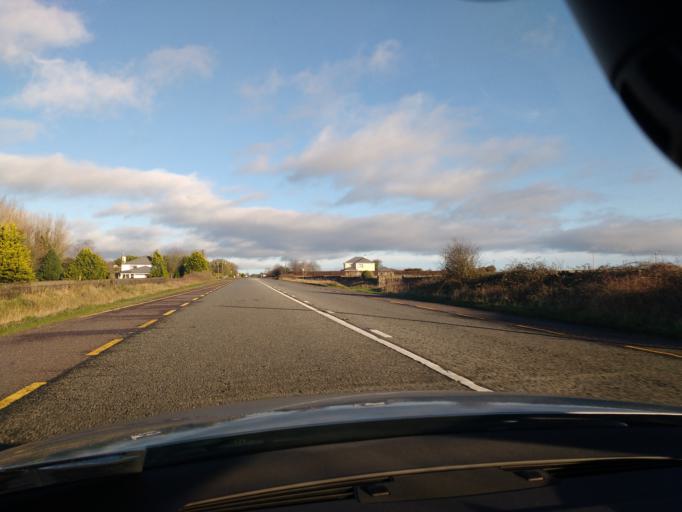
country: IE
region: Leinster
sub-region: Laois
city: Rathdowney
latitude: 52.7002
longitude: -7.6231
